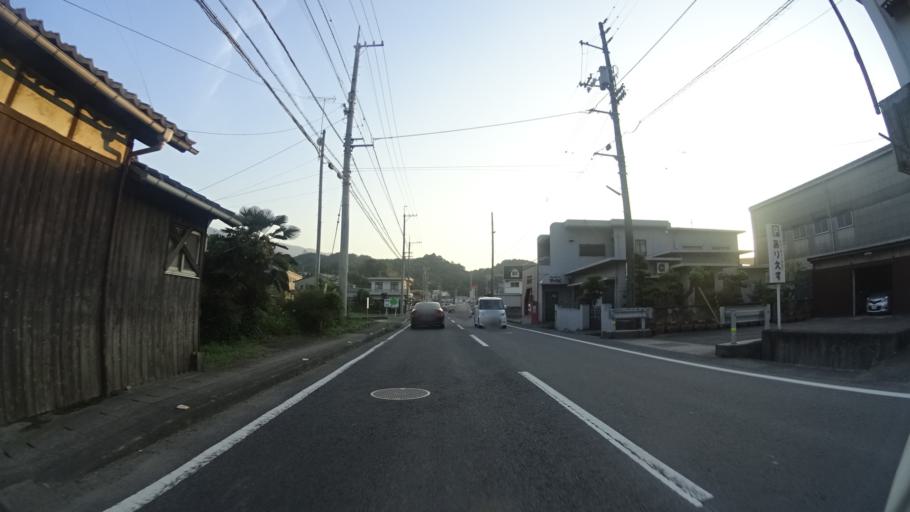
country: JP
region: Ehime
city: Kawanoecho
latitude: 33.9915
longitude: 133.5984
